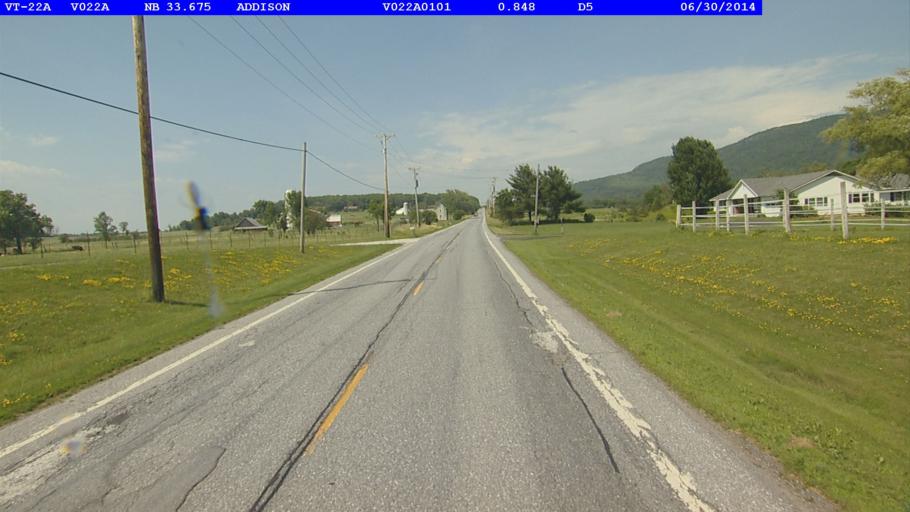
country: US
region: Vermont
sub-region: Addison County
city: Vergennes
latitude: 44.0421
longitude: -73.3051
